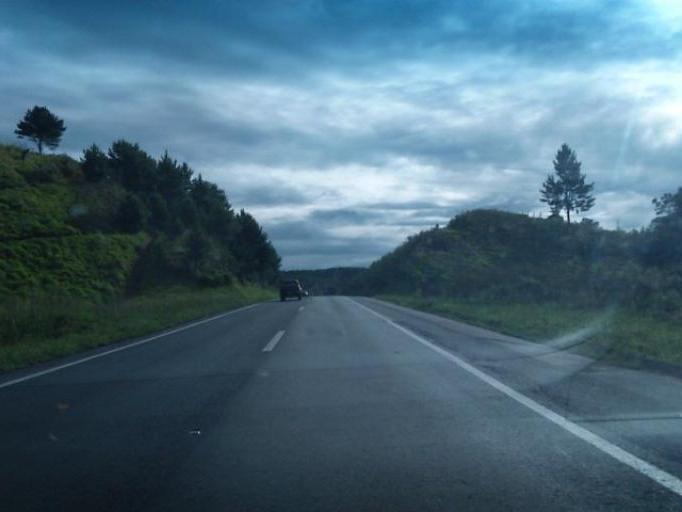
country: BR
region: Parana
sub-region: Campina Grande Do Sul
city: Campina Grande do Sul
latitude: -25.1085
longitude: -48.8512
